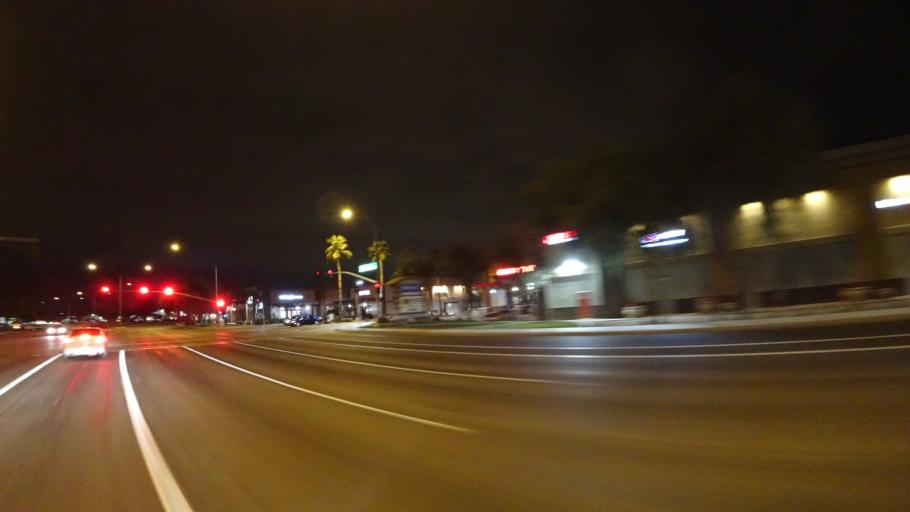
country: US
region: Arizona
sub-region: Pinal County
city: Apache Junction
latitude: 33.3824
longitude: -111.5993
